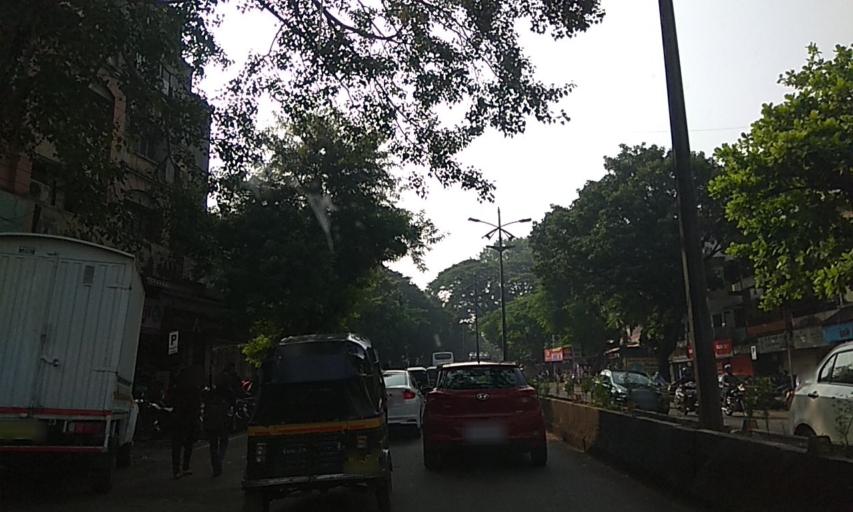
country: IN
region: Maharashtra
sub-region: Pune Division
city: Pune
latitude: 18.5093
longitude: 73.8437
